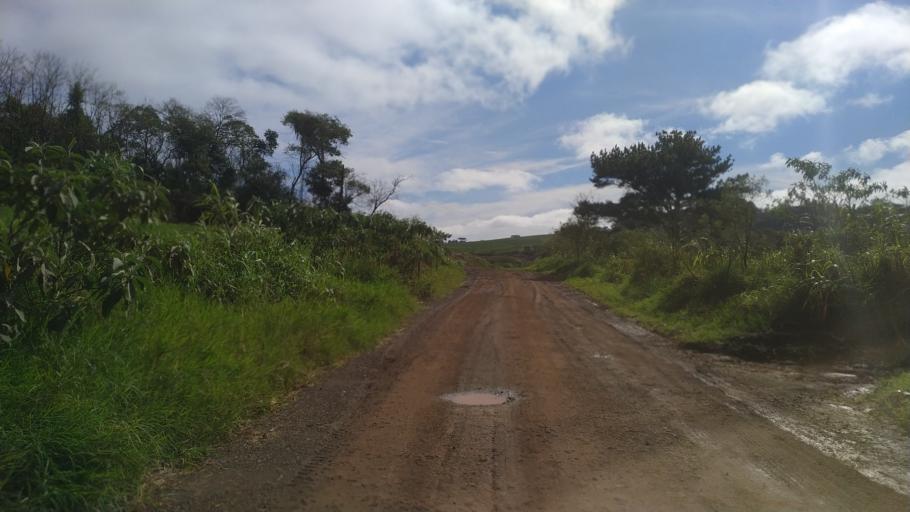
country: BR
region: Santa Catarina
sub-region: Chapeco
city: Chapeco
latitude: -27.1486
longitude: -52.5949
